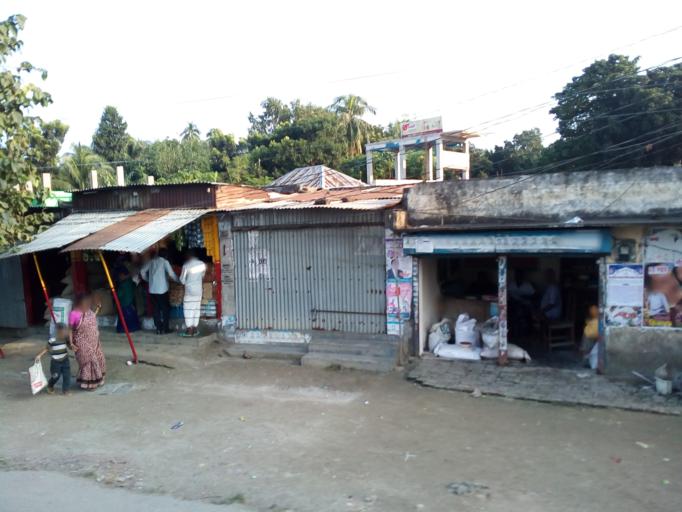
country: BD
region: Dhaka
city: Nagarpur
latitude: 23.8537
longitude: 89.9131
